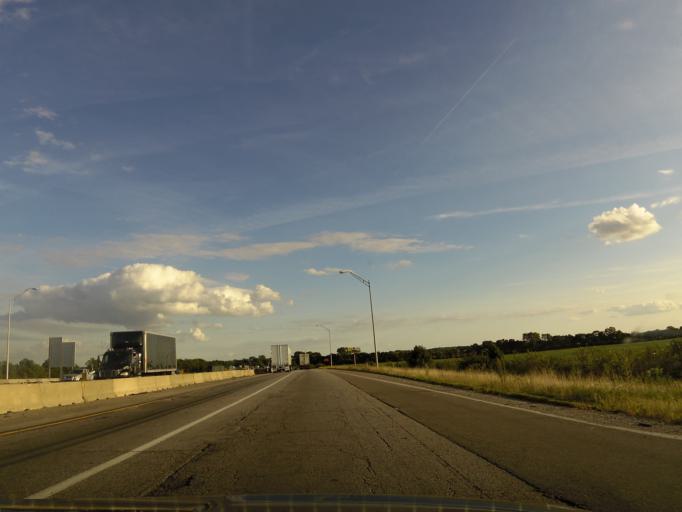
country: US
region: Indiana
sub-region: Tippecanoe County
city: Dayton
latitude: 40.3729
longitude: -86.7839
